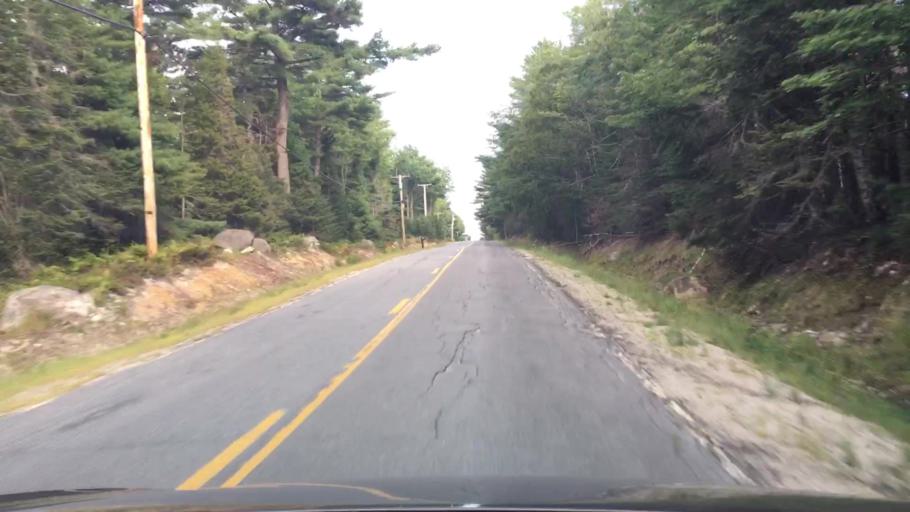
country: US
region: Maine
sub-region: Hancock County
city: Surry
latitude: 44.5000
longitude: -68.5601
